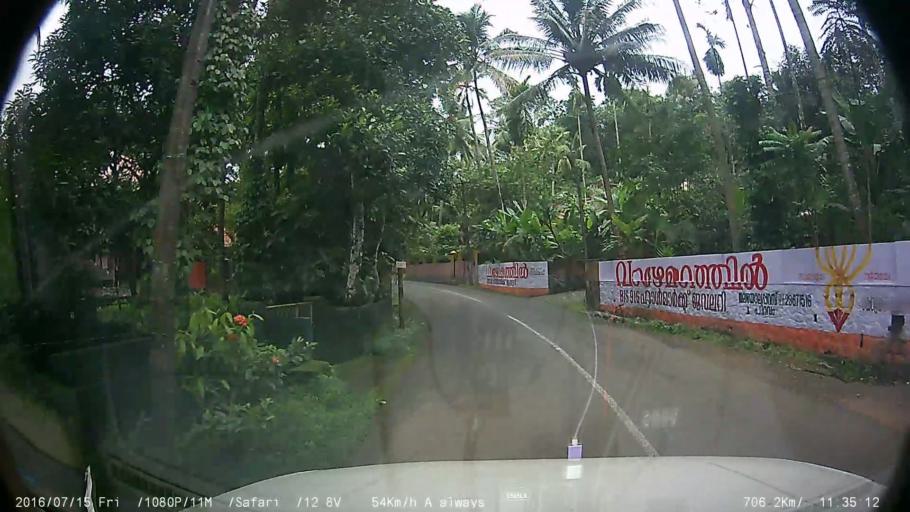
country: IN
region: Kerala
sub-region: Ernakulam
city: Piravam
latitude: 9.7785
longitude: 76.4977
